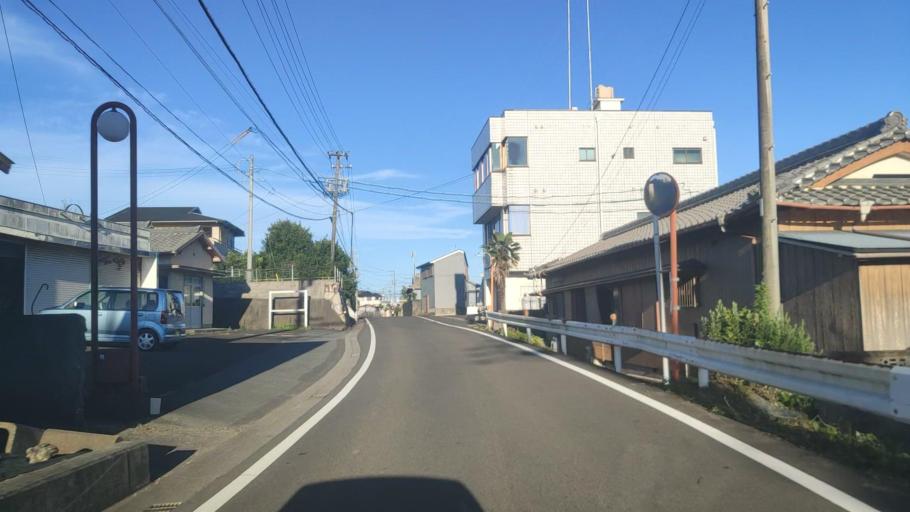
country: JP
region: Mie
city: Toba
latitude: 34.2581
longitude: 136.8170
